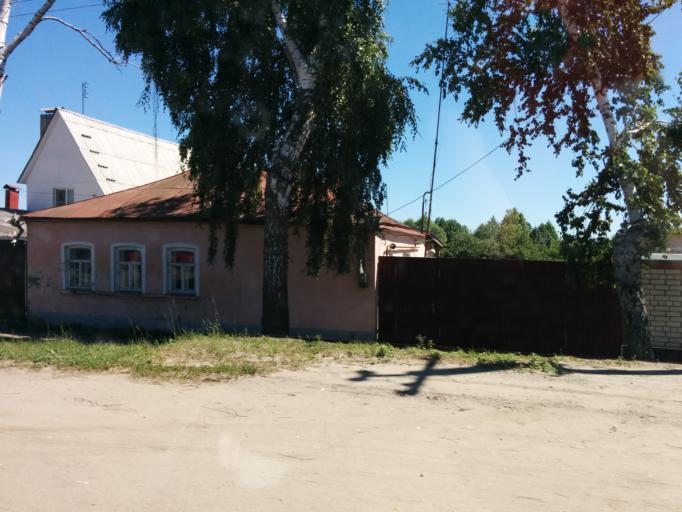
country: RU
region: Tambov
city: Morshansk
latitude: 53.4308
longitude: 41.7937
